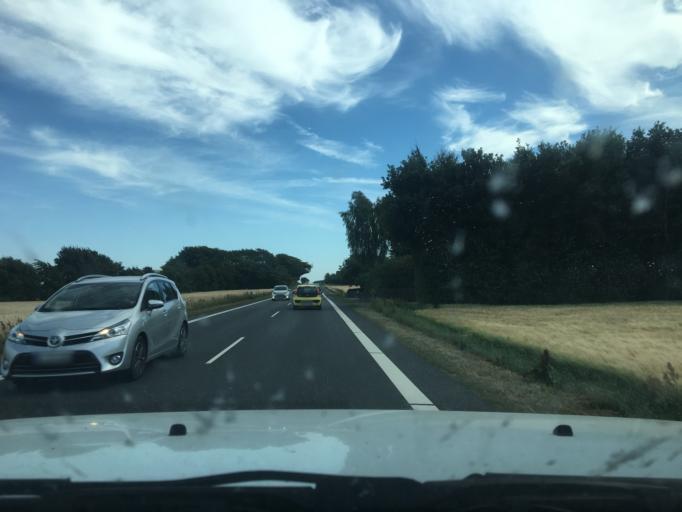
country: DK
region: Central Jutland
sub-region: Viborg Kommune
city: Viborg
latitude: 56.5914
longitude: 9.3660
